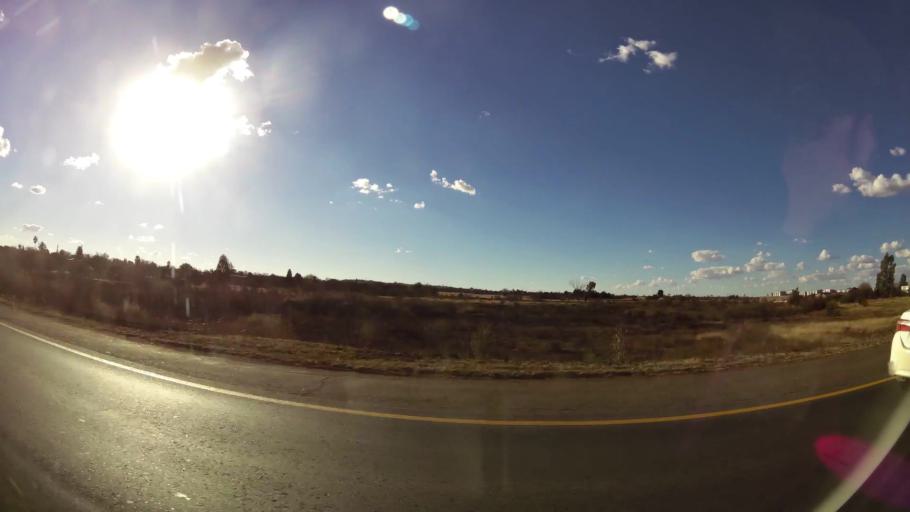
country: ZA
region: North-West
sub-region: Dr Kenneth Kaunda District Municipality
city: Klerksdorp
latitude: -26.8488
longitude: 26.6981
